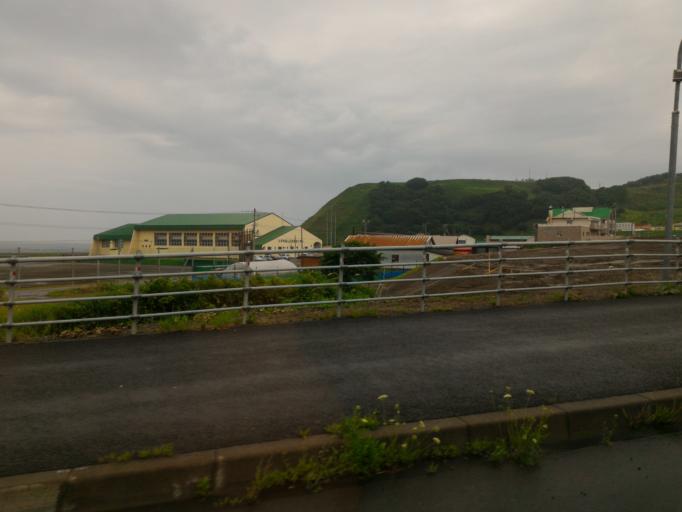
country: JP
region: Hokkaido
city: Rumoi
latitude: 44.0256
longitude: 141.6667
